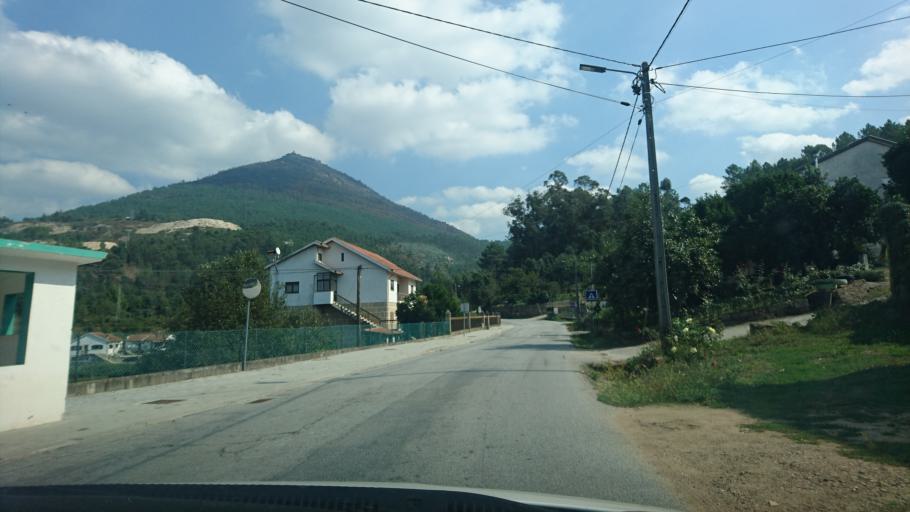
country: PT
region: Vila Real
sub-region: Mondim de Basto
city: Mondim de Basto
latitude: 41.4182
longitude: -7.9432
